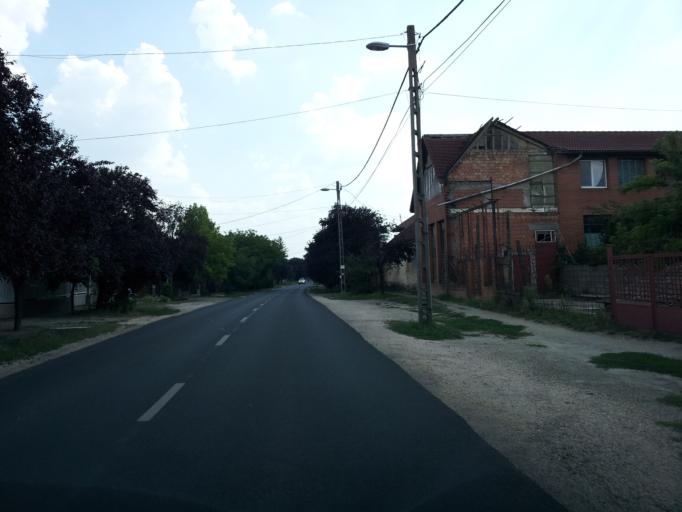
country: HU
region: Pest
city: Toekoel
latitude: 47.3327
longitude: 18.9653
